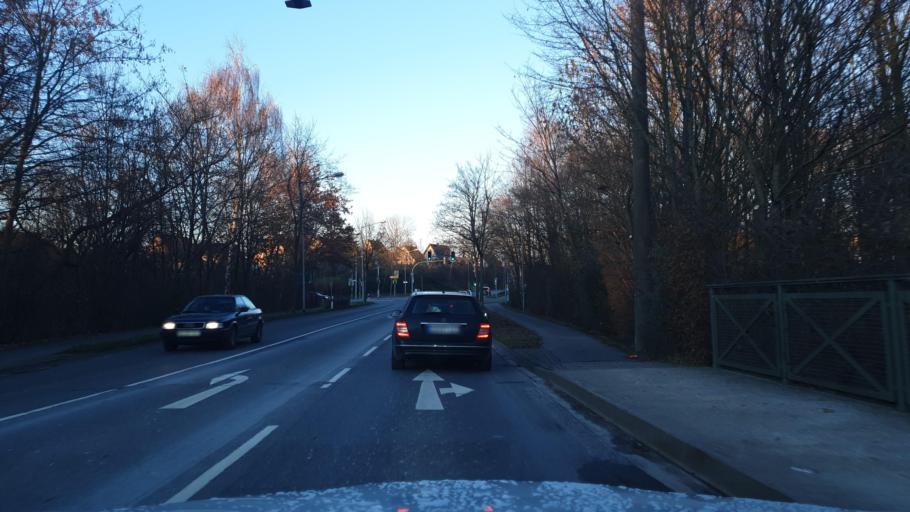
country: DE
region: North Rhine-Westphalia
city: Bad Oeynhausen
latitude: 52.2185
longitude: 8.8184
